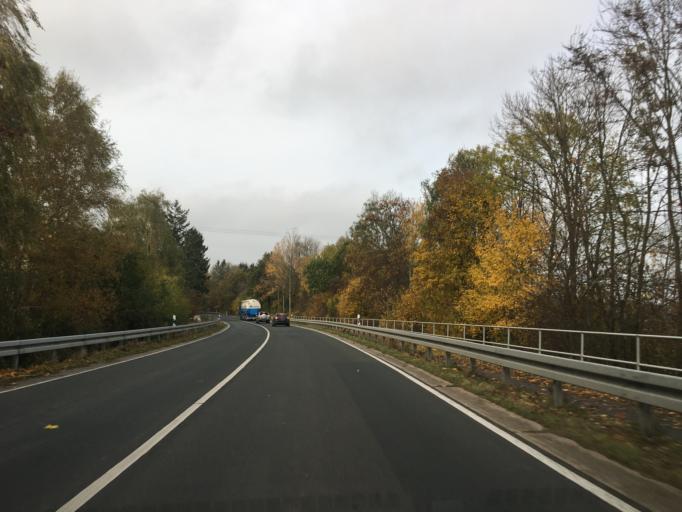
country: DE
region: North Rhine-Westphalia
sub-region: Regierungsbezirk Munster
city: Altenberge
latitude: 52.0531
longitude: 7.4646
